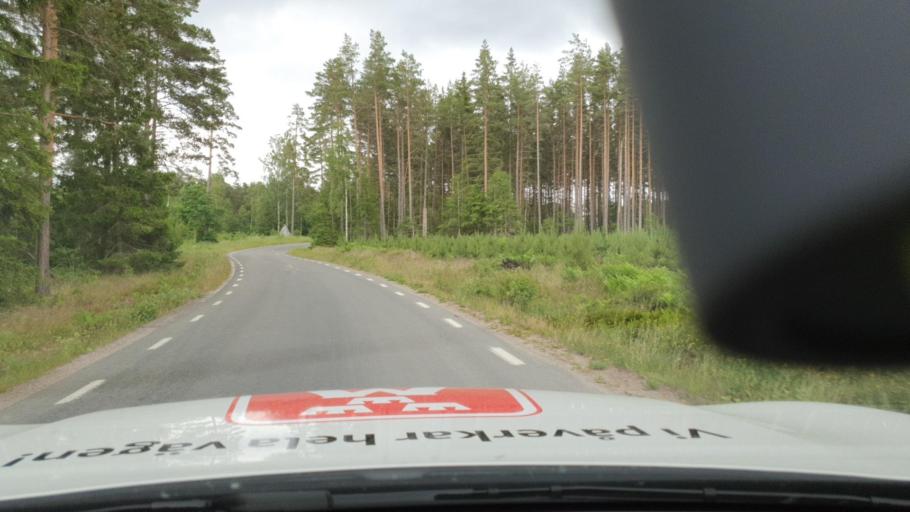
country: SE
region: Vaestra Goetaland
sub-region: Tidaholms Kommun
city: Olofstorp
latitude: 58.1759
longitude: 14.1504
